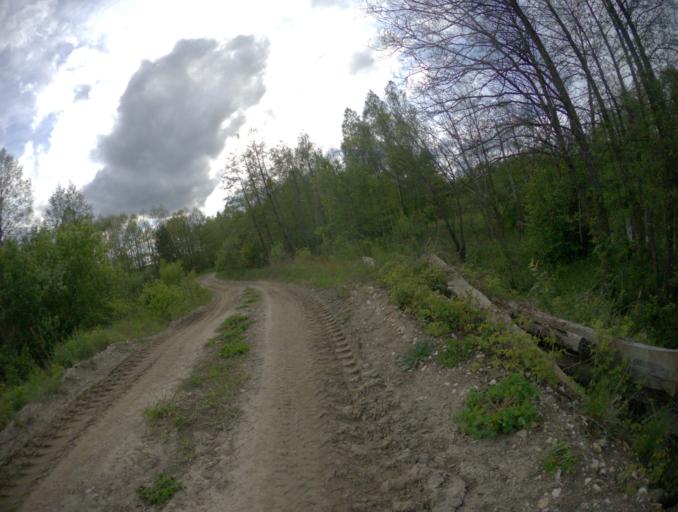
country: RU
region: Rjazan
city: Gus'-Zheleznyy
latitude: 55.1332
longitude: 41.1049
